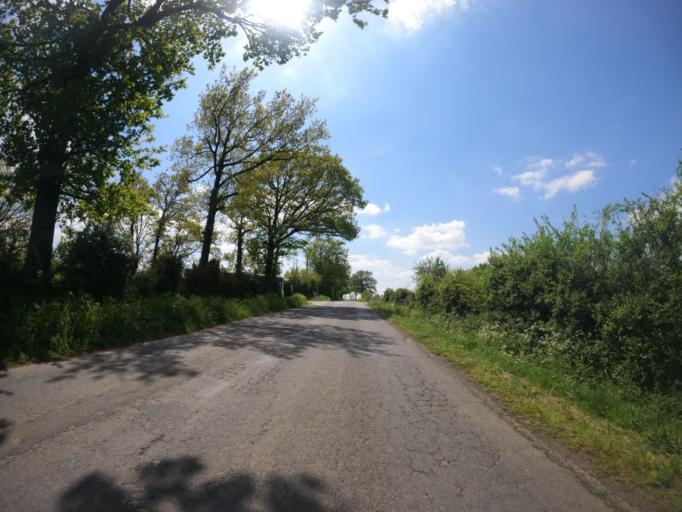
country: FR
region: Poitou-Charentes
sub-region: Departement des Deux-Sevres
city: Chiche
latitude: 46.7283
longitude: -0.3781
